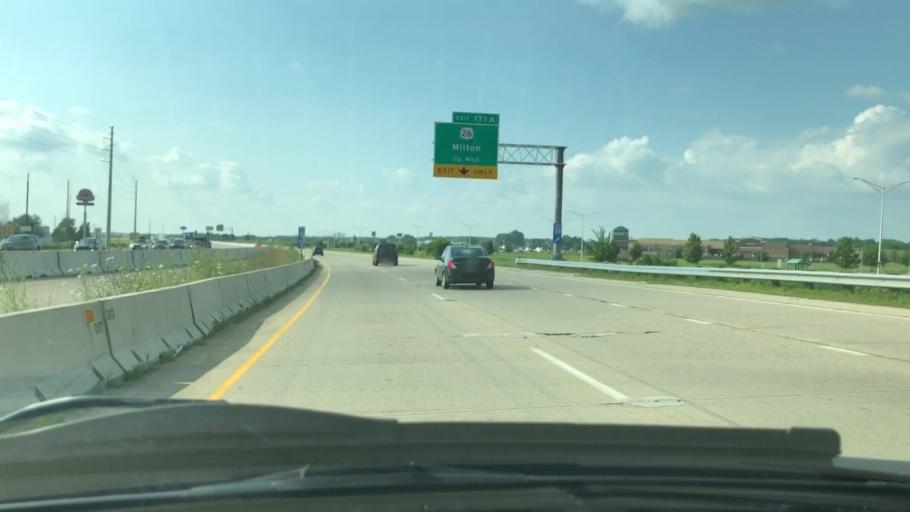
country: US
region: Wisconsin
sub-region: Rock County
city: Janesville
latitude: 42.7203
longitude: -88.9861
